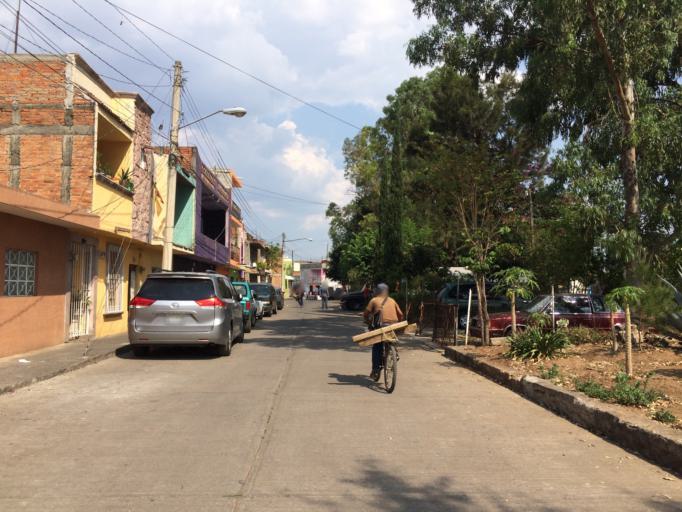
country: MX
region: Michoacan
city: Morelia
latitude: 19.7090
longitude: -101.2096
